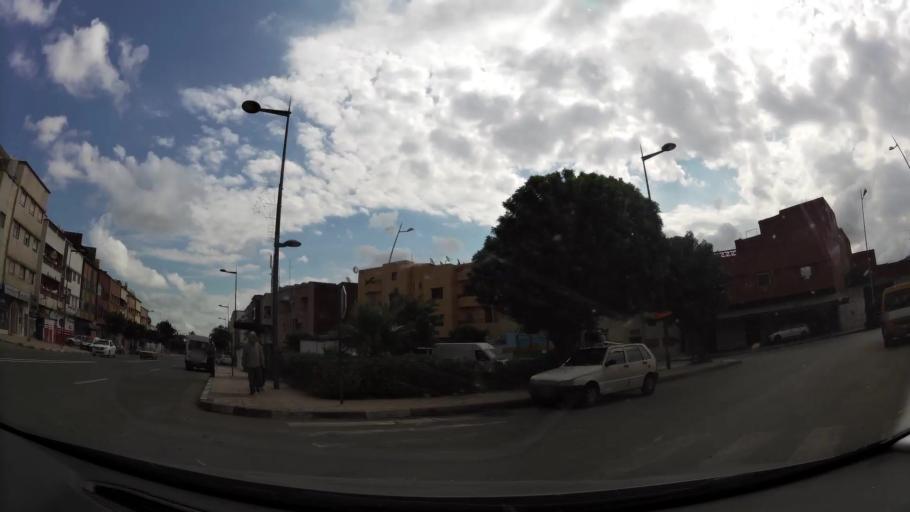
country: MA
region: Gharb-Chrarda-Beni Hssen
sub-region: Kenitra Province
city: Kenitra
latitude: 34.2711
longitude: -6.5592
